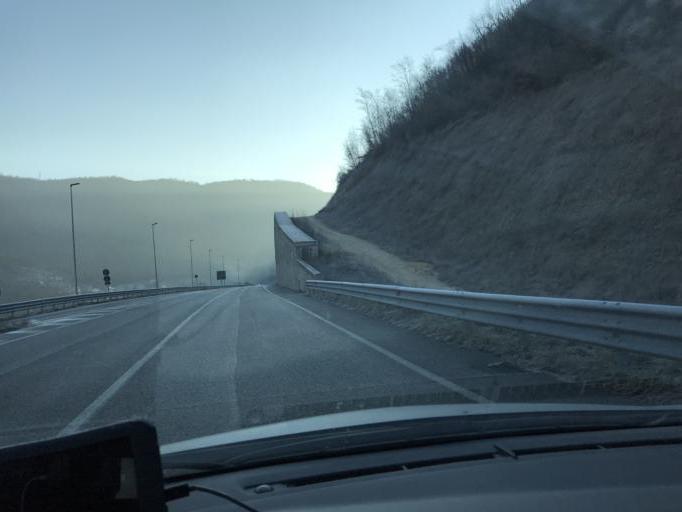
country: IT
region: Latium
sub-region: Provincia di Rieti
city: Cittaducale
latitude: 42.3523
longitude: 12.9555
